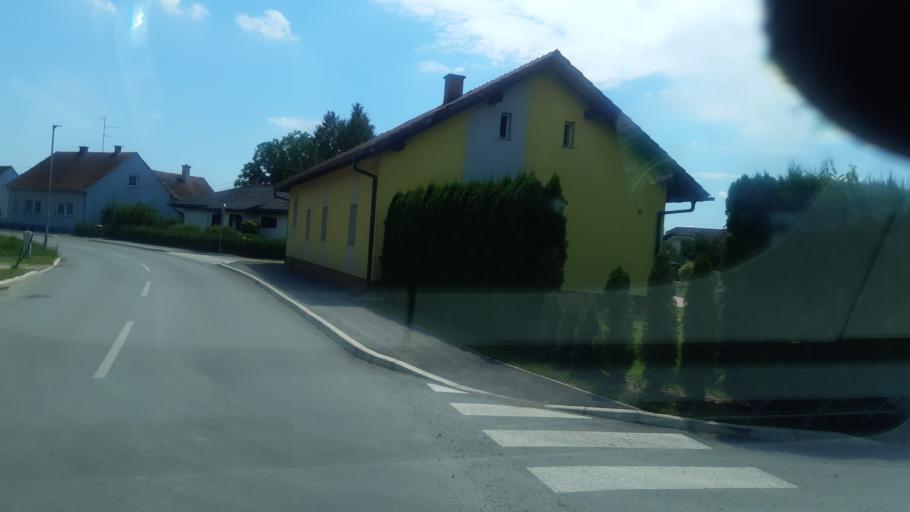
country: SI
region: Moravske Toplice
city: Moravske Toplice
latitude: 46.6832
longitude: 16.1917
